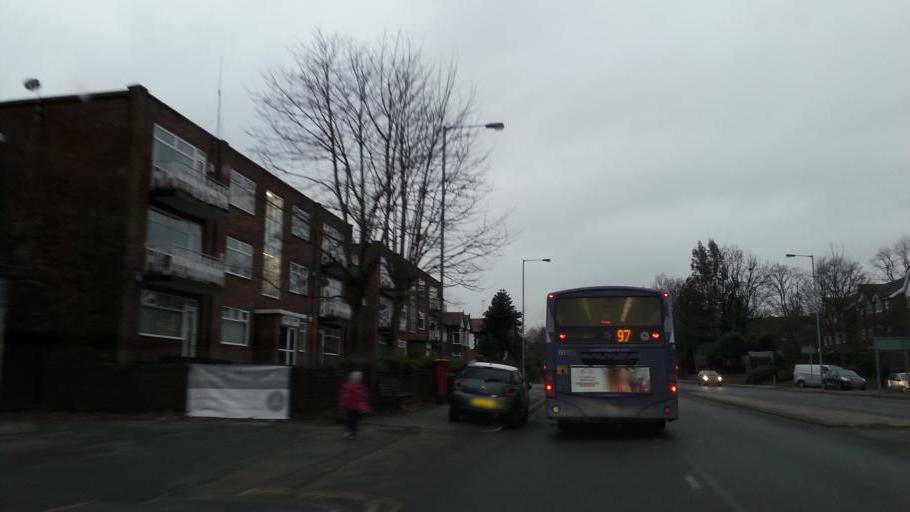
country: GB
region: England
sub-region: Borough of Bury
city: Prestwich
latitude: 53.5237
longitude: -2.2766
